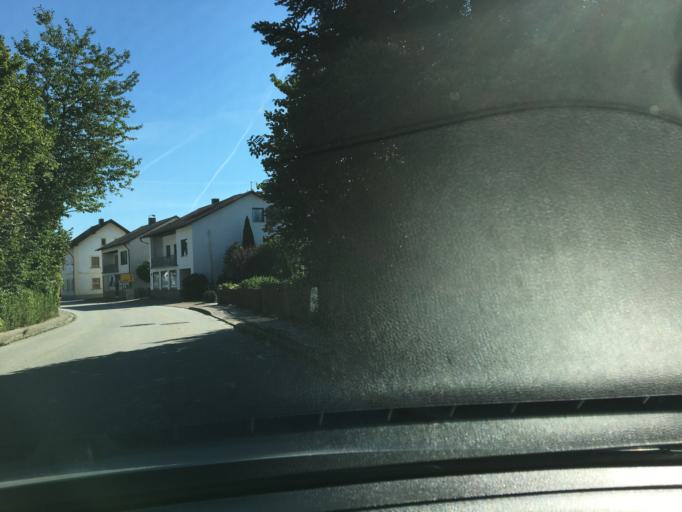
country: DE
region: Bavaria
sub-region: Lower Bavaria
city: Bodenkirchen
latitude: 48.3822
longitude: 12.3843
